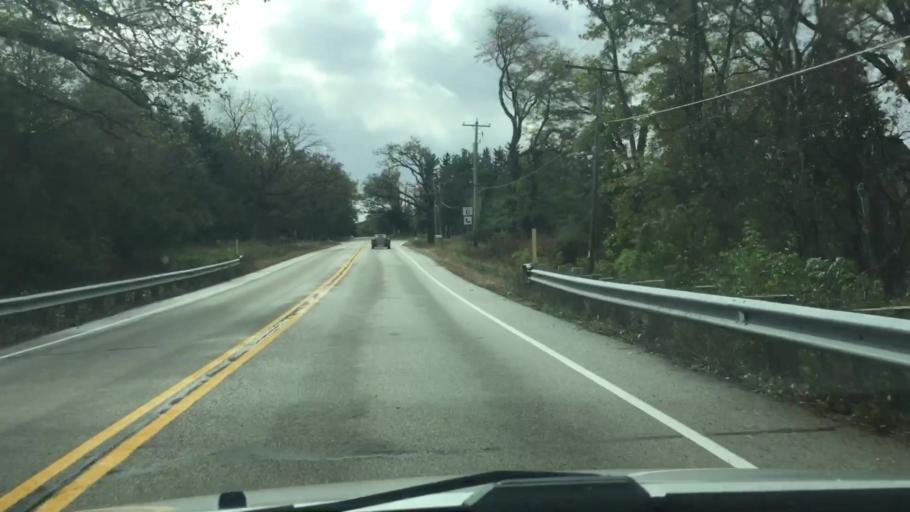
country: US
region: Wisconsin
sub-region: Waukesha County
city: Dousman
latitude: 42.9902
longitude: -88.4636
